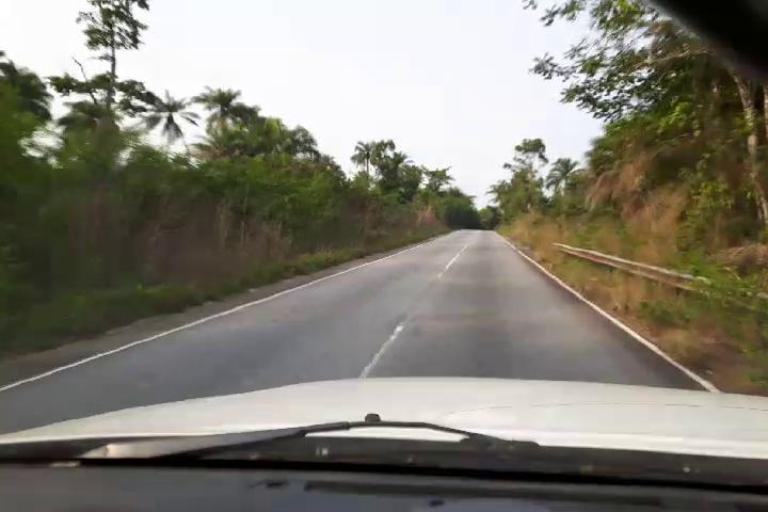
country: SL
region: Southern Province
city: Palima
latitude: 7.9310
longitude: -11.5306
